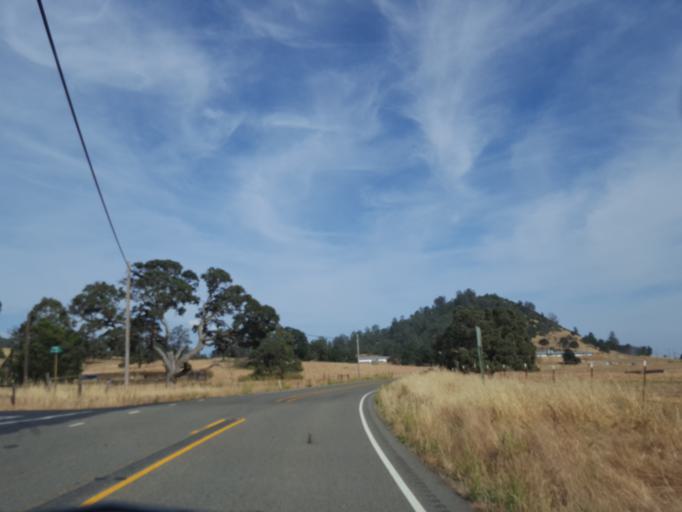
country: US
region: California
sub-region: Tuolumne County
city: Jamestown
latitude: 37.8322
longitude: -120.4791
